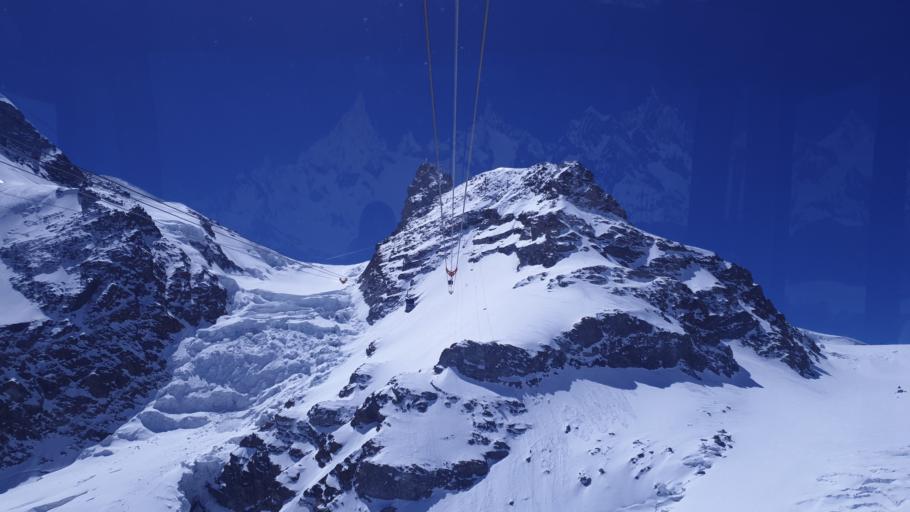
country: CH
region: Valais
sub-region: Visp District
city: Zermatt
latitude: 45.9534
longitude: 7.7256
